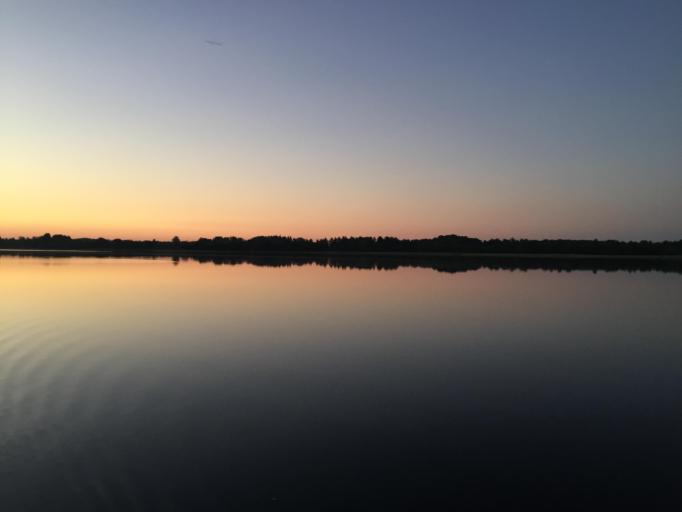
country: LV
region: Rezekne
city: Rezekne
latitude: 56.3631
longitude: 27.4224
